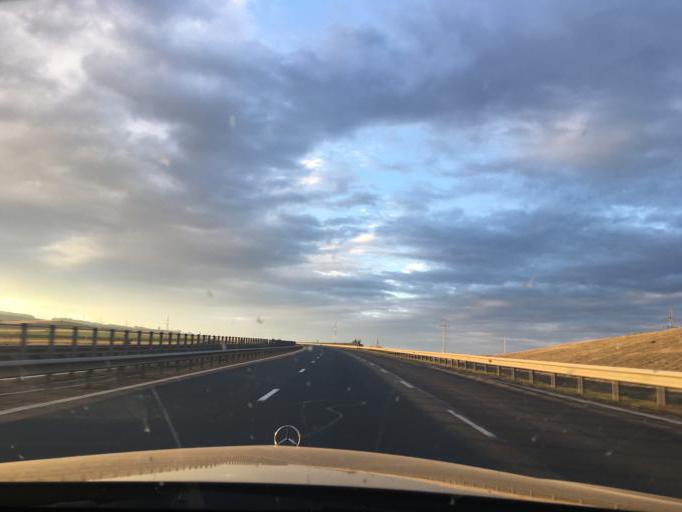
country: RO
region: Cluj
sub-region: Comuna Sandulesti
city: Copaceni
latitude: 46.5823
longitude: 23.7374
